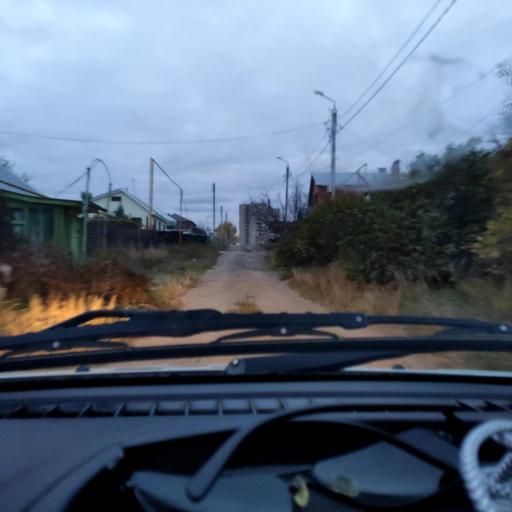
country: RU
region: Samara
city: Zhigulevsk
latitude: 53.4838
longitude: 49.5239
